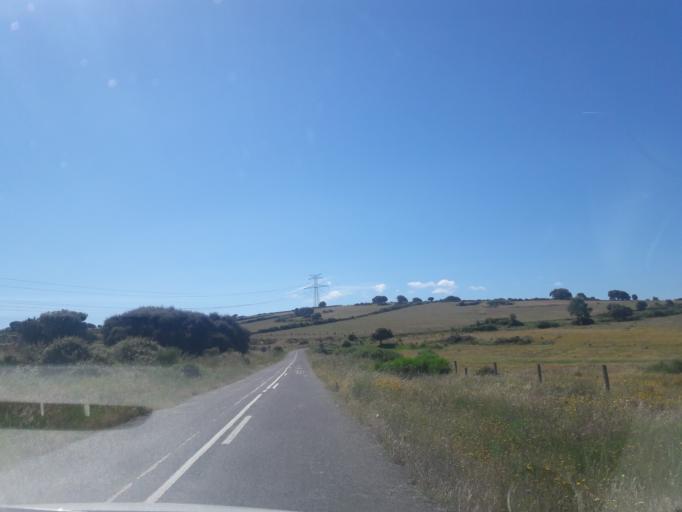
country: ES
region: Castille and Leon
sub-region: Provincia de Salamanca
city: Lumbrales
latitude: 40.9884
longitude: -6.7293
